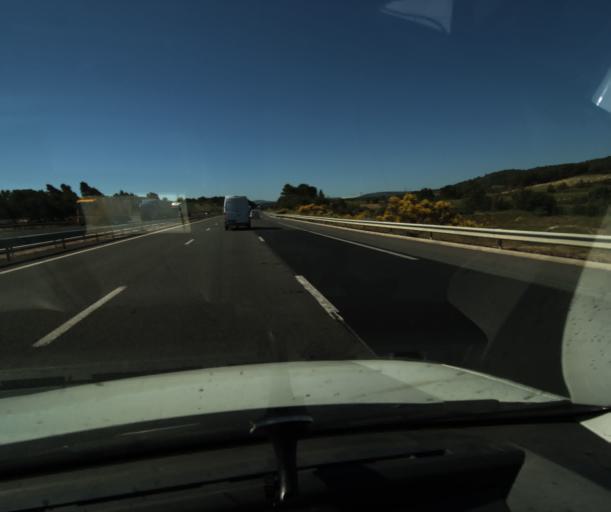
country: FR
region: Languedoc-Roussillon
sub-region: Departement de l'Aude
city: Peyriac-de-Mer
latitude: 43.0883
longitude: 2.9386
